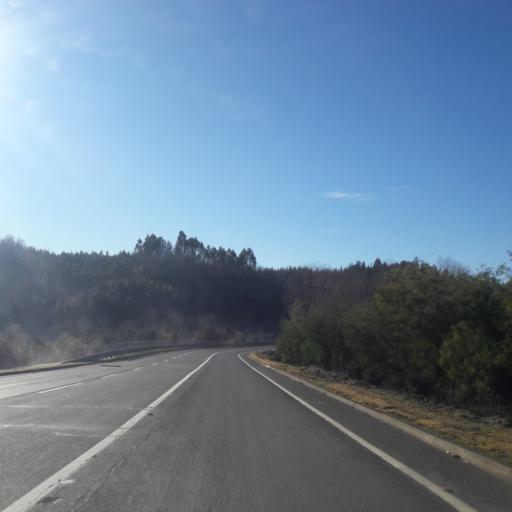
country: CL
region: Biobio
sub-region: Provincia de Biobio
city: La Laja
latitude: -37.2730
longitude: -72.9536
